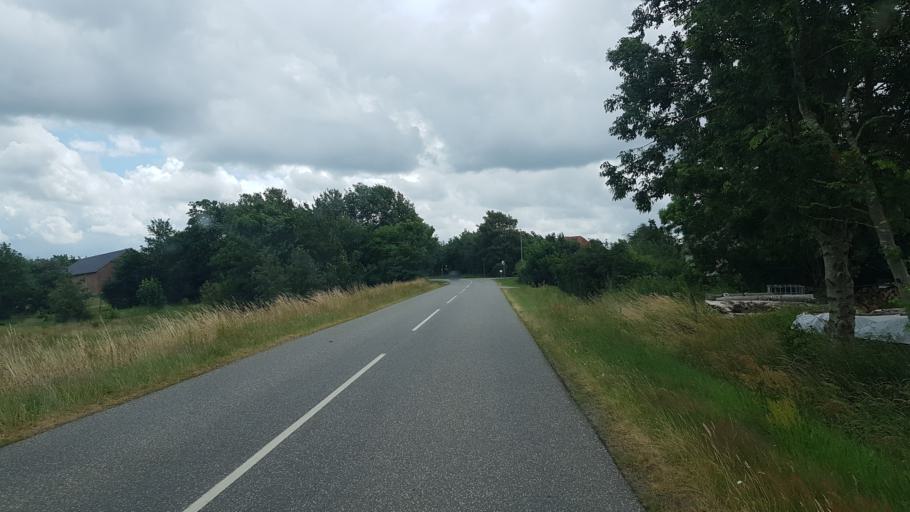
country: DK
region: South Denmark
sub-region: Kolding Kommune
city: Vamdrup
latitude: 55.4343
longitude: 9.2636
